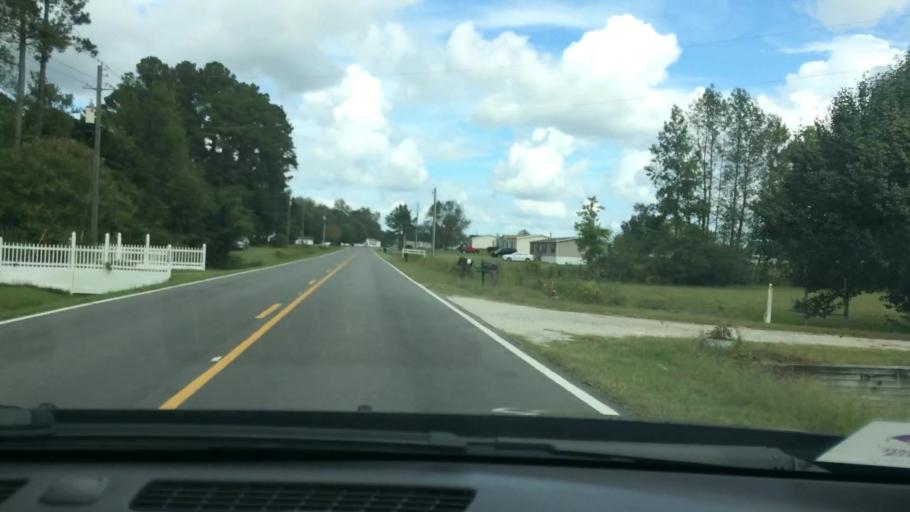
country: US
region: North Carolina
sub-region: Pitt County
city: Ayden
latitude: 35.4621
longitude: -77.4656
